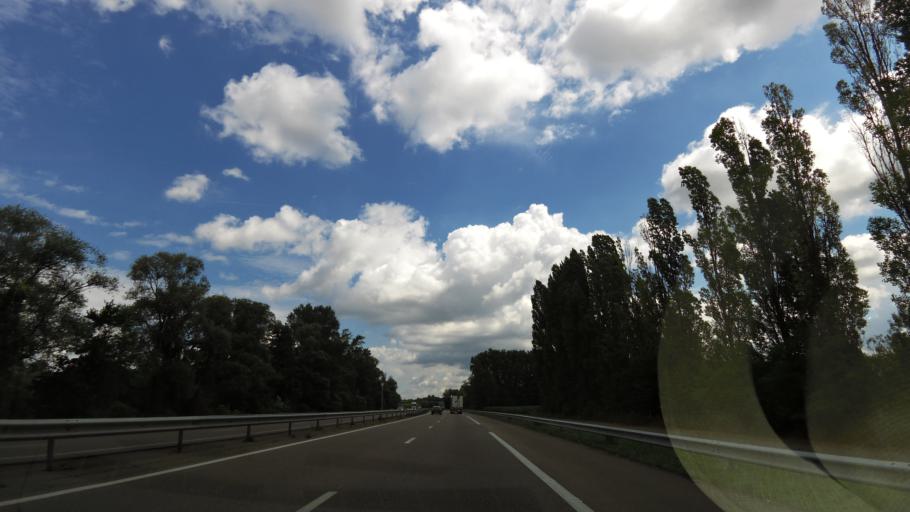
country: FR
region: Alsace
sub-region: Departement du Bas-Rhin
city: Roppenheim
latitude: 48.8455
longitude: 8.0412
